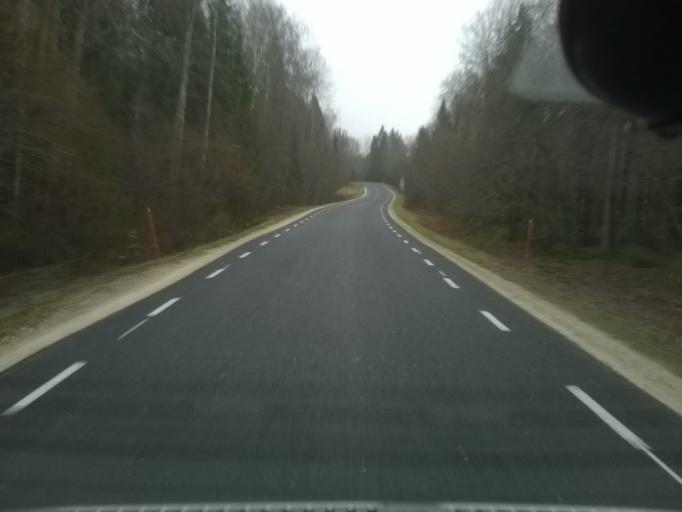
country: EE
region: Harju
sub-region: Saue linn
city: Saue
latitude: 59.1407
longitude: 24.5206
